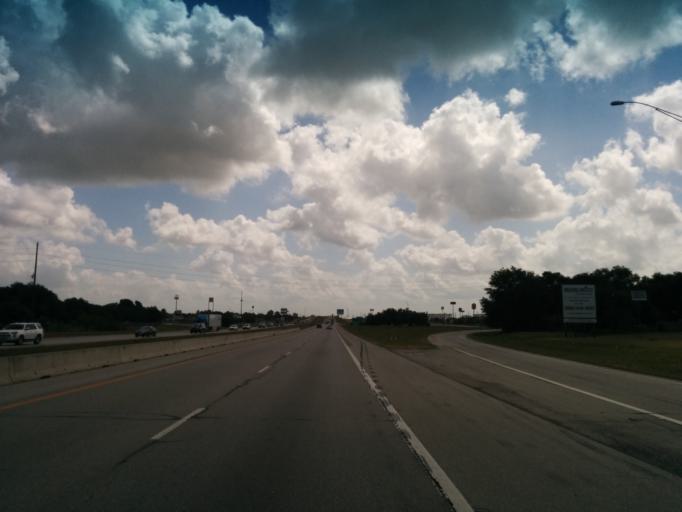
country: US
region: Texas
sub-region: Austin County
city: Sealy
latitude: 29.7619
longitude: -96.1607
